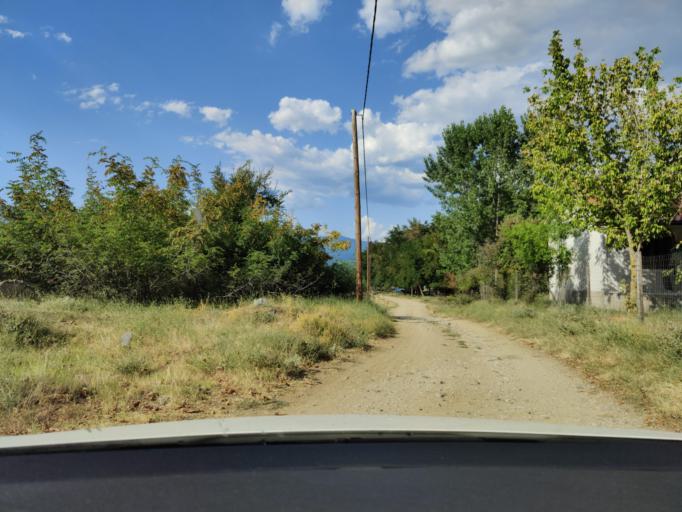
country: GR
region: Central Macedonia
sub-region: Nomos Serron
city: Chrysochorafa
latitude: 41.1822
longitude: 23.1061
